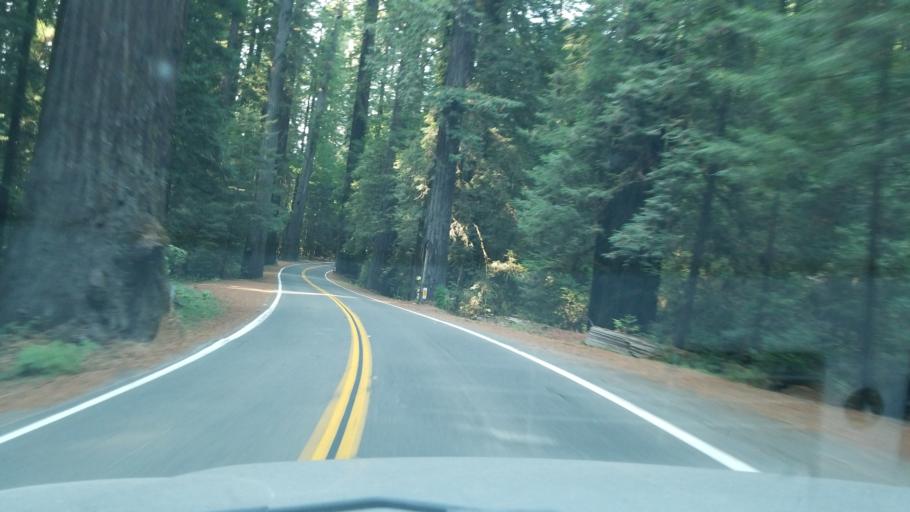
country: US
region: California
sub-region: Humboldt County
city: Redway
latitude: 40.2427
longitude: -123.8208
